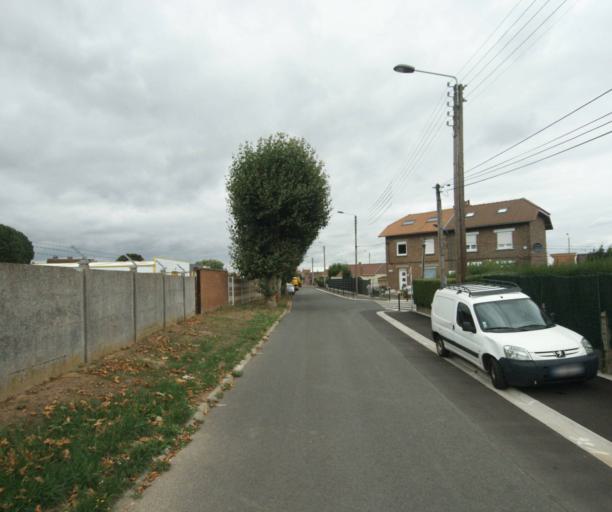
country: FR
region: Nord-Pas-de-Calais
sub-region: Departement du Nord
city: Lesquin
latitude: 50.5893
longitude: 3.1241
